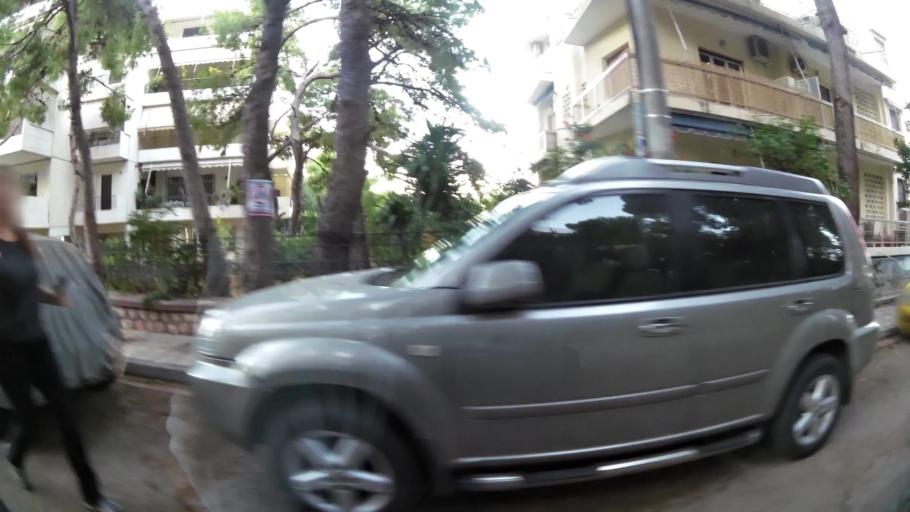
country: GR
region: Attica
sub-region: Nomarchia Anatolikis Attikis
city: Vouliagmeni
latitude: 37.8154
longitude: 23.7969
